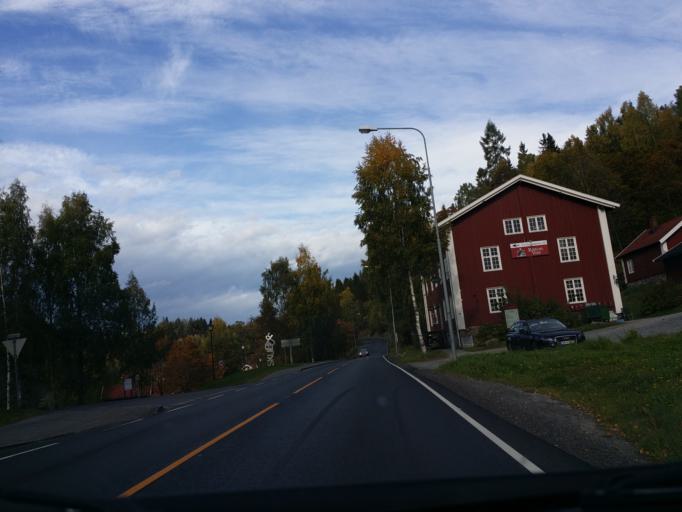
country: NO
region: Akershus
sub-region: Baerum
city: Sandvika
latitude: 59.9374
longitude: 10.5017
